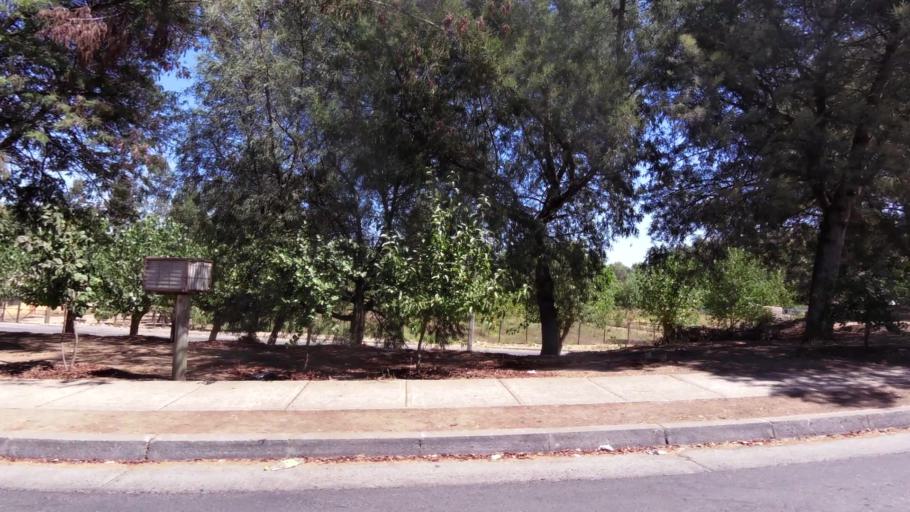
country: CL
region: Maule
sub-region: Provincia de Talca
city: Talca
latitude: -35.3092
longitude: -71.5114
